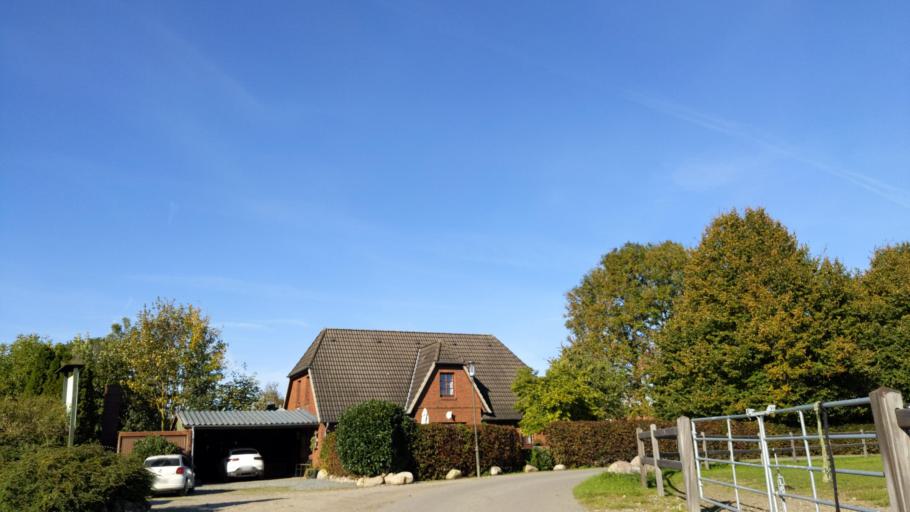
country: DE
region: Schleswig-Holstein
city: Ahrensbok
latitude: 54.0169
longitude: 10.6198
